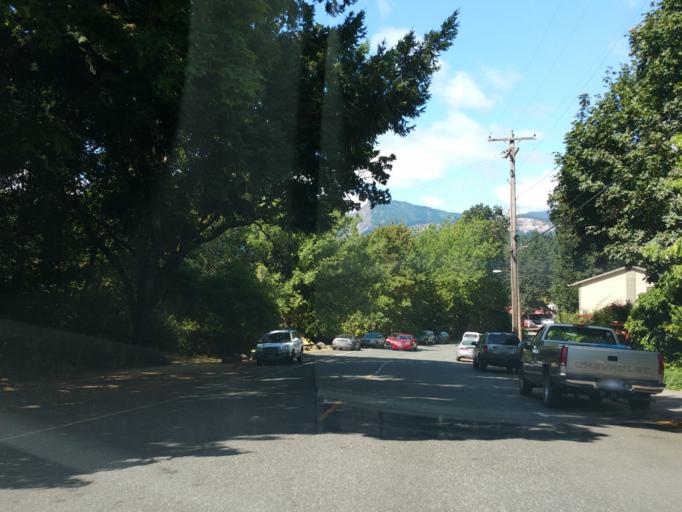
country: US
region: Washington
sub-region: Skamania County
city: Stevenson
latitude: 45.6928
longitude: -121.8879
